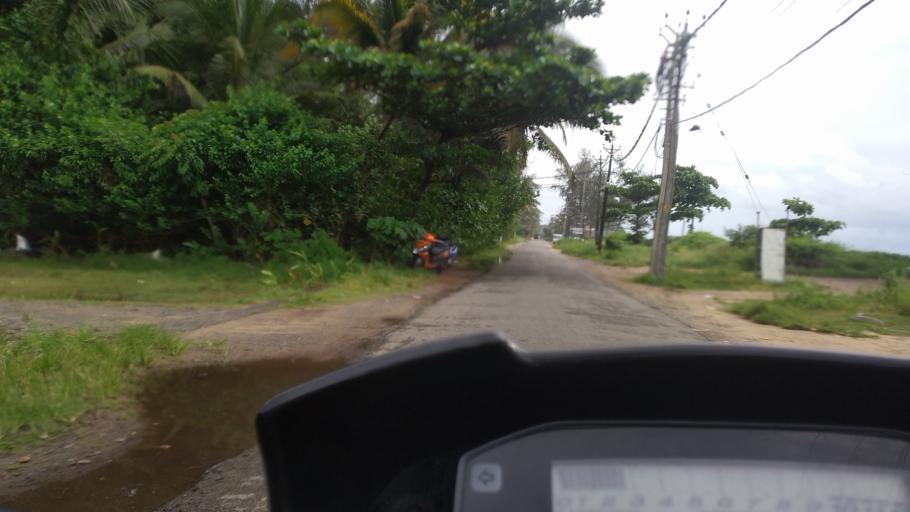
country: IN
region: Kerala
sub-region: Thrissur District
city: Kodungallur
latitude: 10.1502
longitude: 76.1757
